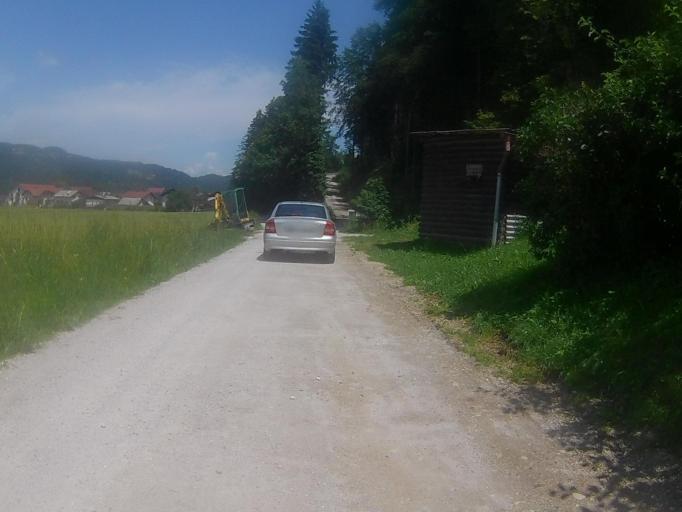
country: SI
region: Ruse
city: Bistrica ob Dravi
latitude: 46.5451
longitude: 15.5341
